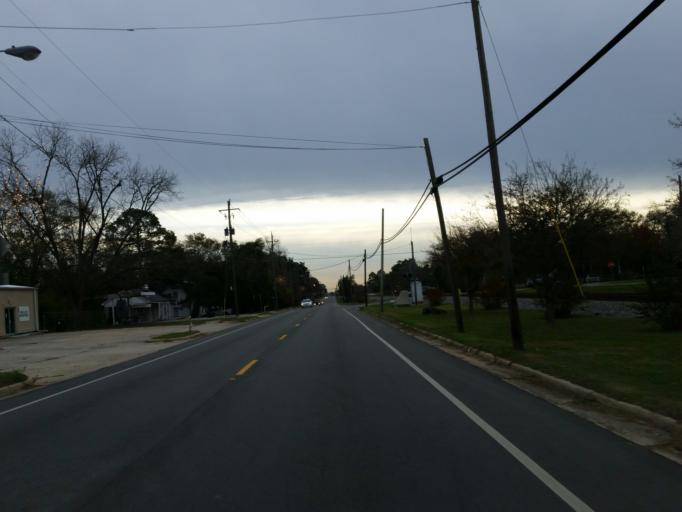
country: US
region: Georgia
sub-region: Turner County
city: Ashburn
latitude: 31.7025
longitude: -83.6518
